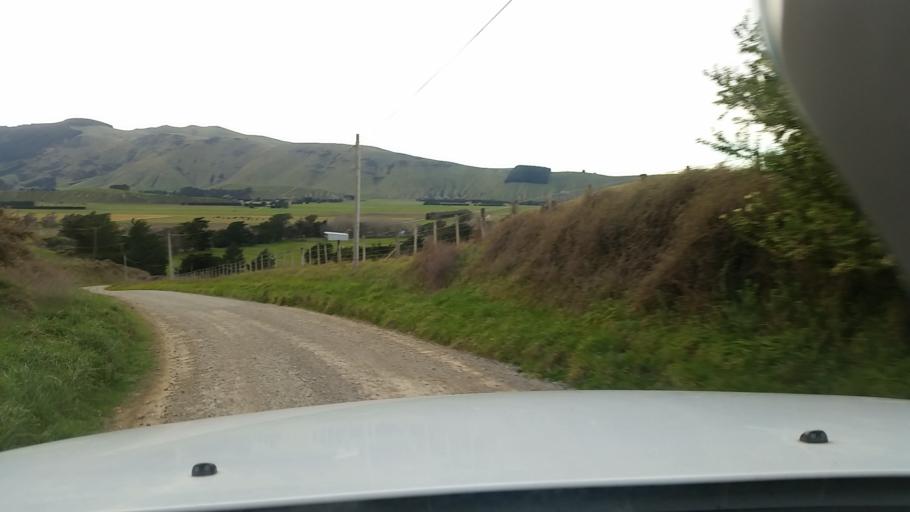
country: NZ
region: Canterbury
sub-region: Selwyn District
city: Lincoln
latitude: -43.7201
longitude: 172.5896
